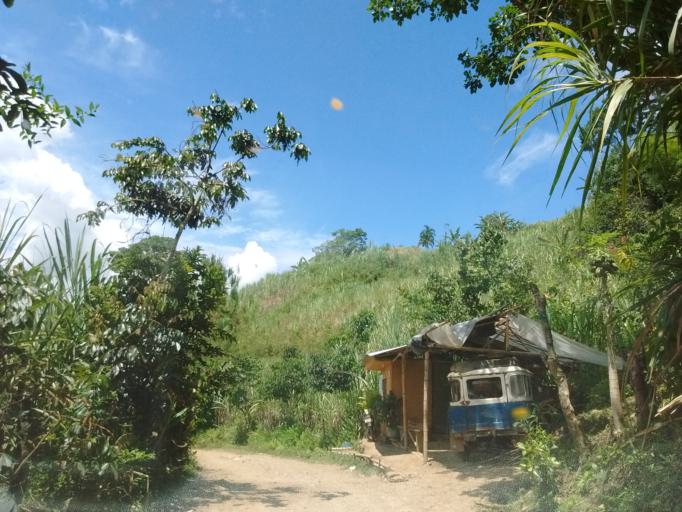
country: CO
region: Cauca
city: Villa Rica
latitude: 2.6582
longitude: -76.7680
